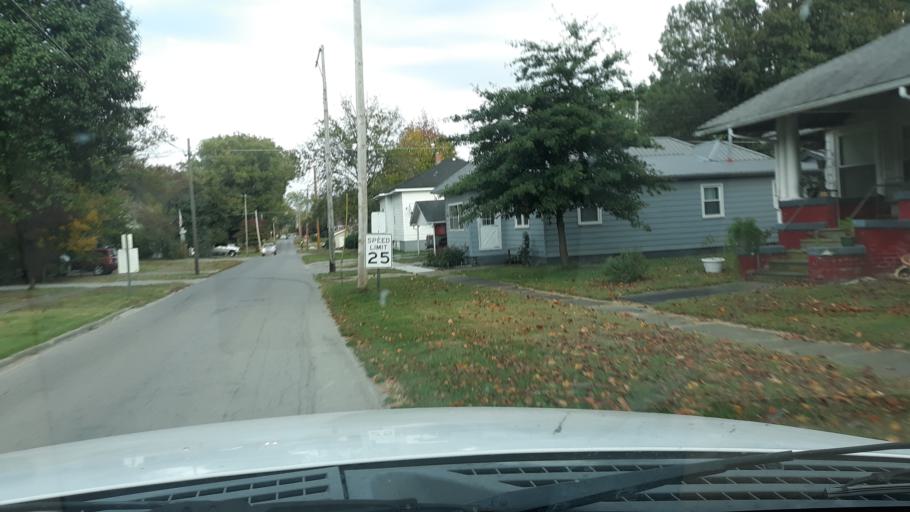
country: US
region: Illinois
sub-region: Saline County
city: Eldorado
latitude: 37.8161
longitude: -88.4415
